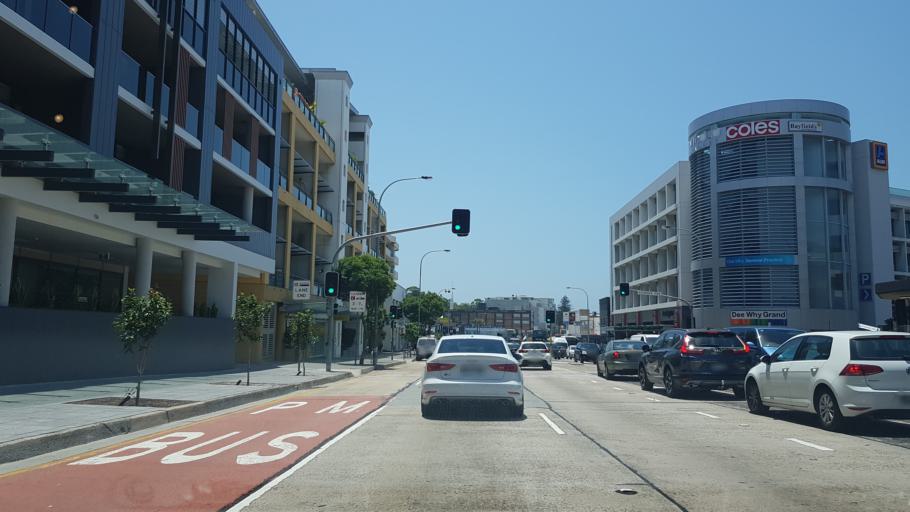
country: AU
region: New South Wales
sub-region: Warringah
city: Narraweena
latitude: -33.7555
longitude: 151.2832
